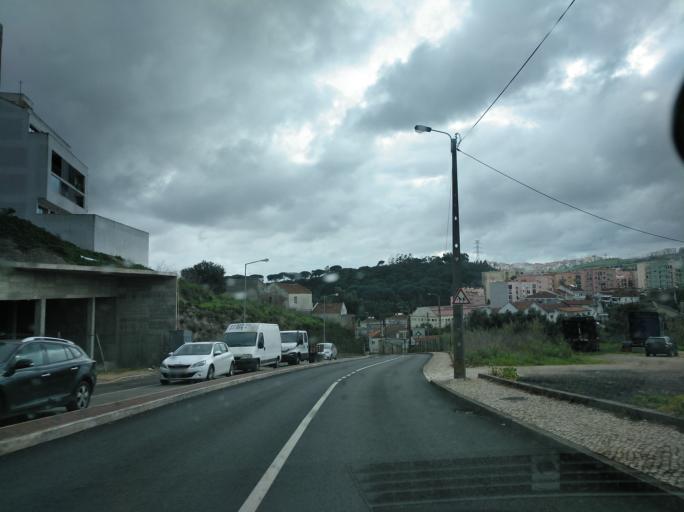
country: PT
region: Lisbon
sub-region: Odivelas
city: Famoes
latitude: 38.7834
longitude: -9.2071
